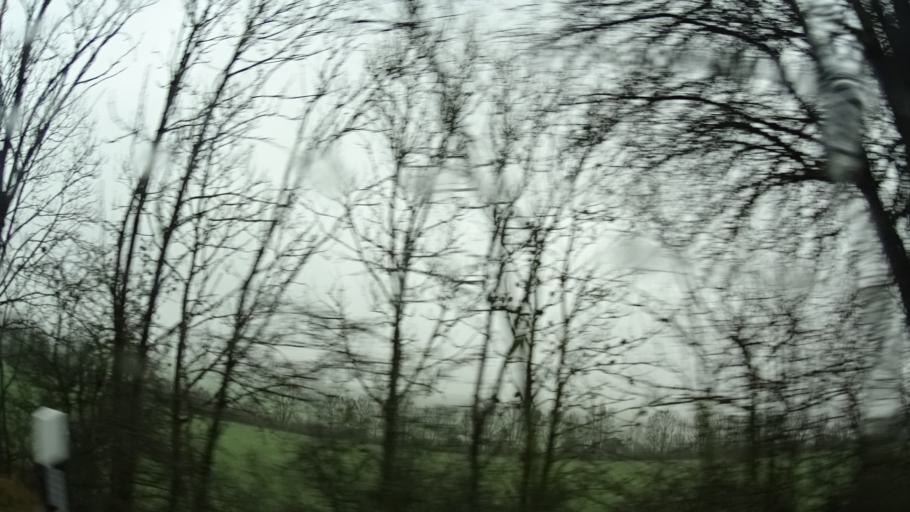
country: DE
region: Thuringia
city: Eisfeld
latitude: 50.4545
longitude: 10.9027
